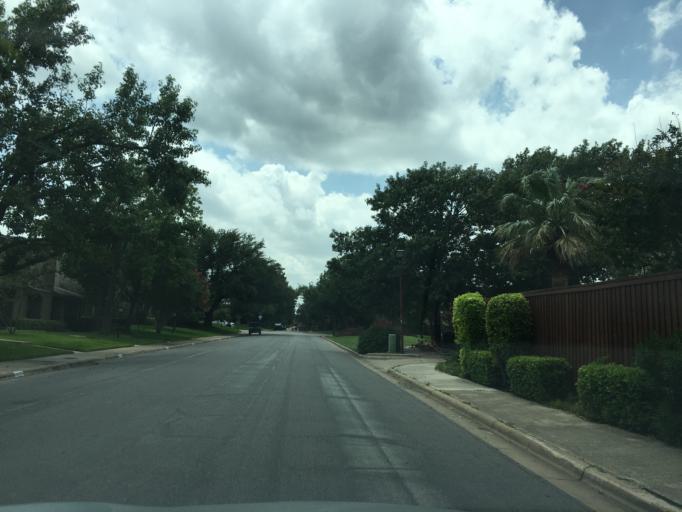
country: US
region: Texas
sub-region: Dallas County
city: University Park
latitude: 32.8937
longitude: -96.7775
